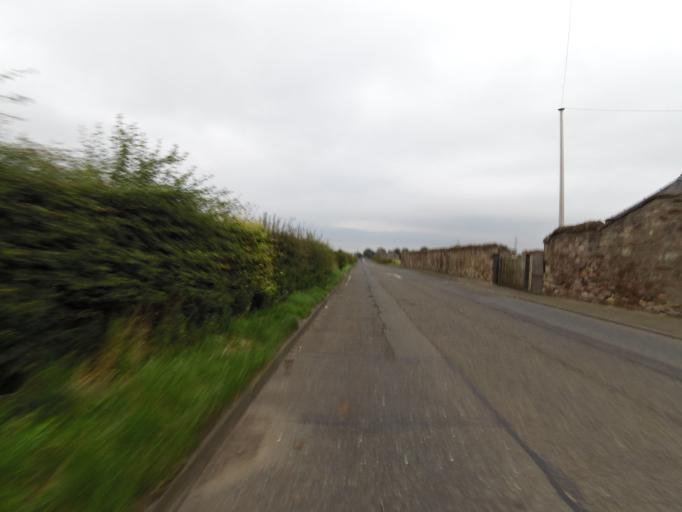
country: GB
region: Scotland
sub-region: Midlothian
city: Dalkeith
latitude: 55.9172
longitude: -3.0754
